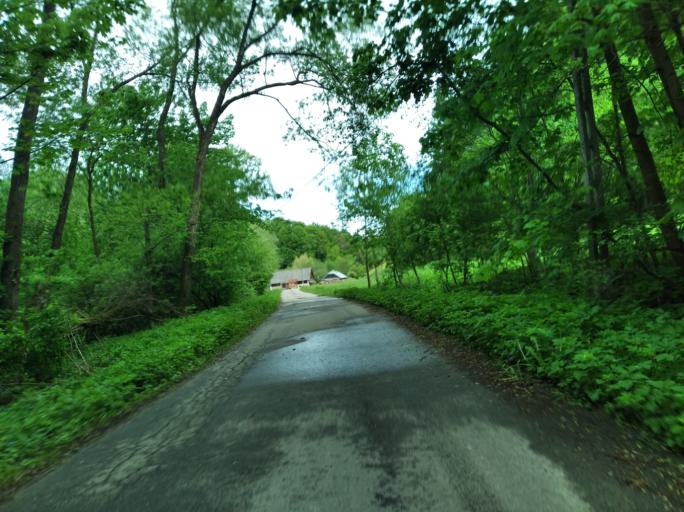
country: PL
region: Subcarpathian Voivodeship
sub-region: Powiat strzyzowski
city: Strzyzow
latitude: 49.9183
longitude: 21.7562
